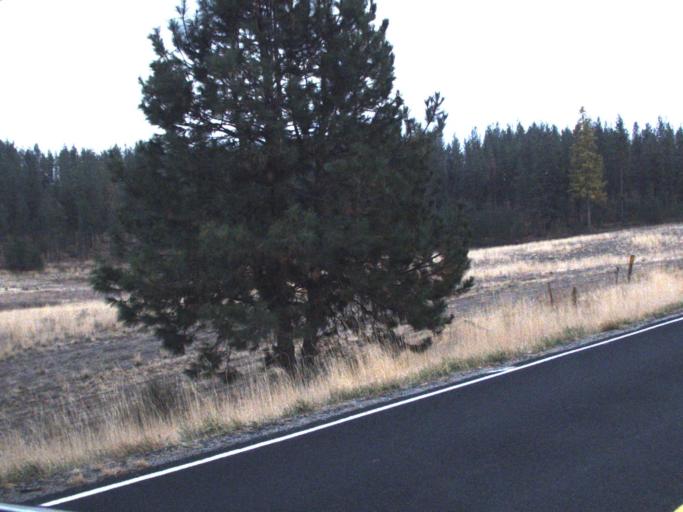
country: US
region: Washington
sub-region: Lincoln County
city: Davenport
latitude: 48.0202
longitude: -118.2364
